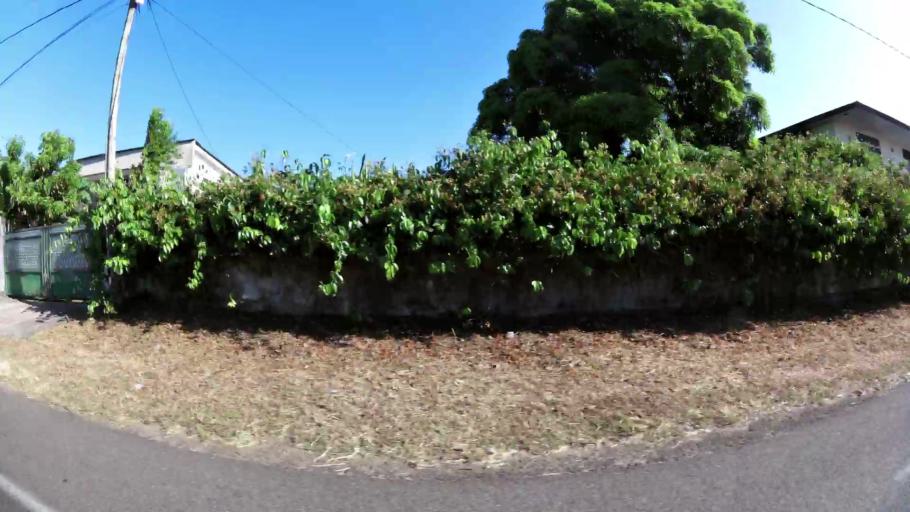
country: GF
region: Guyane
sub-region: Guyane
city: Remire-Montjoly
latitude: 4.8876
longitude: -52.2790
